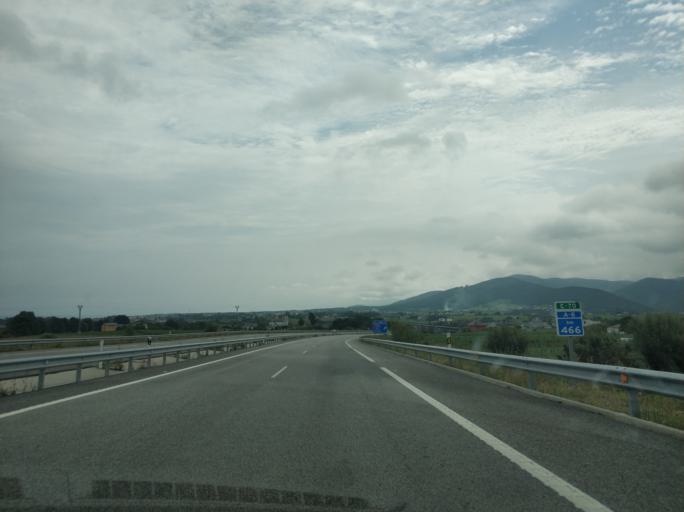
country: ES
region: Asturias
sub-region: Province of Asturias
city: Navia
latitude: 43.5291
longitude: -6.5666
